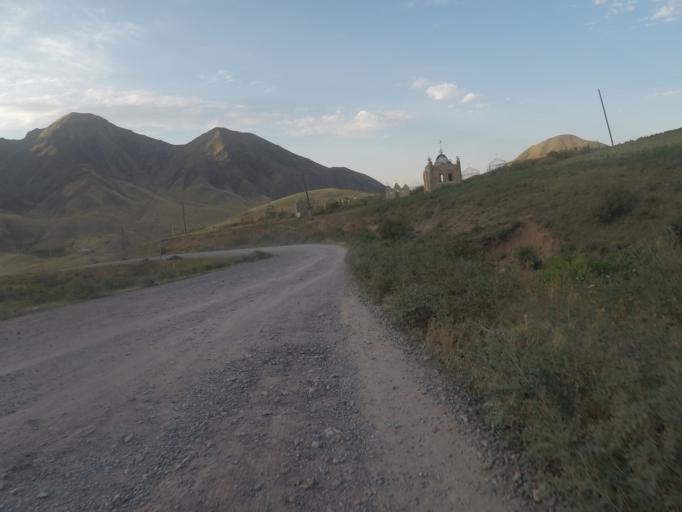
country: KG
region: Chuy
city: Bishkek
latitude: 42.6678
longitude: 74.6477
